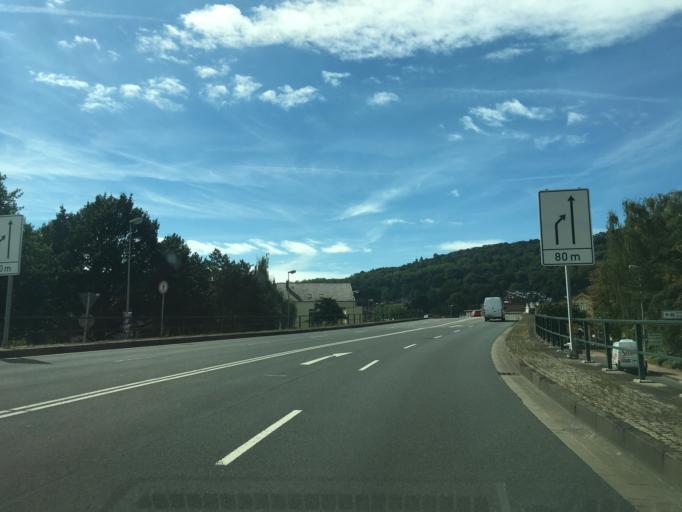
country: DE
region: Lower Saxony
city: Hameln
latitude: 52.1028
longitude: 9.3492
